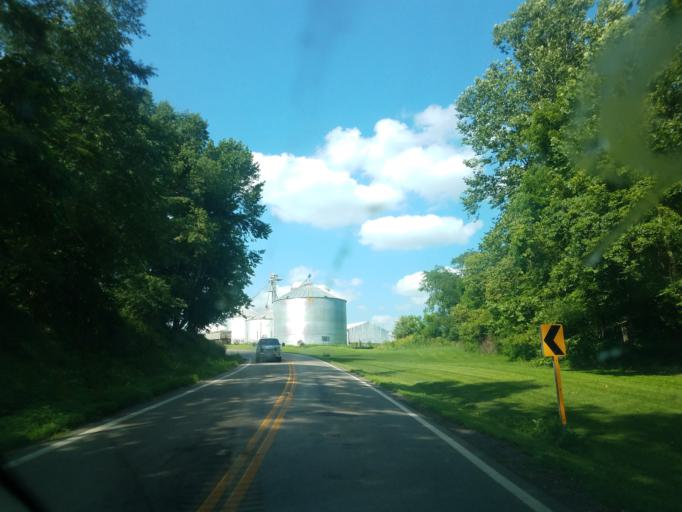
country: US
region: Ohio
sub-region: Knox County
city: Danville
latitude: 40.5162
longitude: -82.2032
